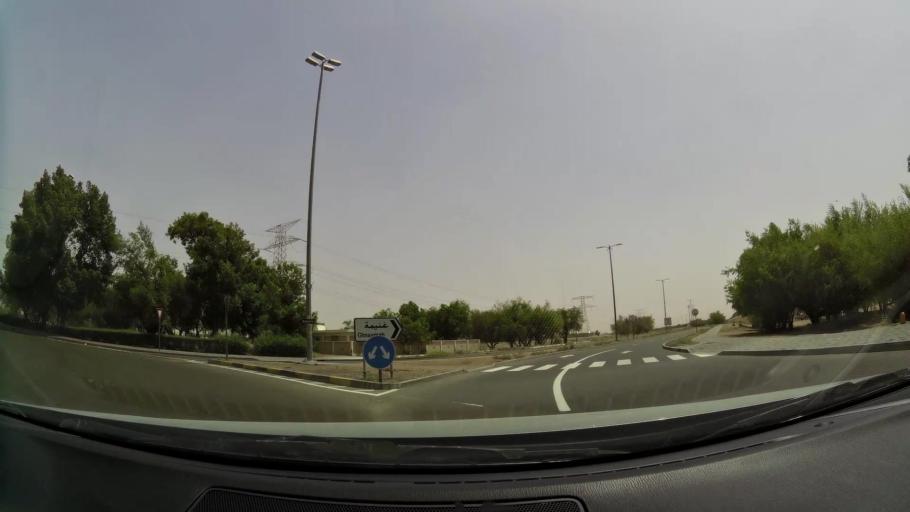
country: AE
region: Abu Dhabi
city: Al Ain
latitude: 24.1751
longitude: 55.6636
